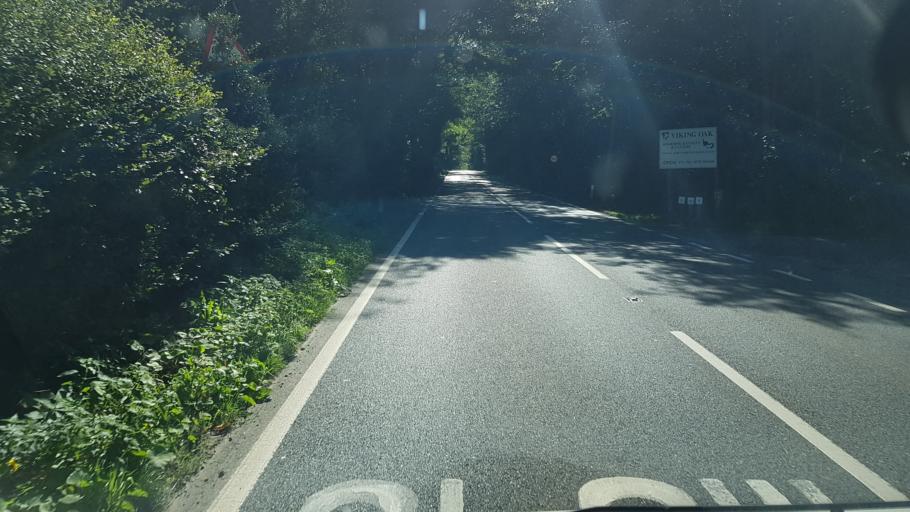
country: GB
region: England
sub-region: Kent
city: Kings Hill
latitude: 51.2788
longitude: 0.3530
